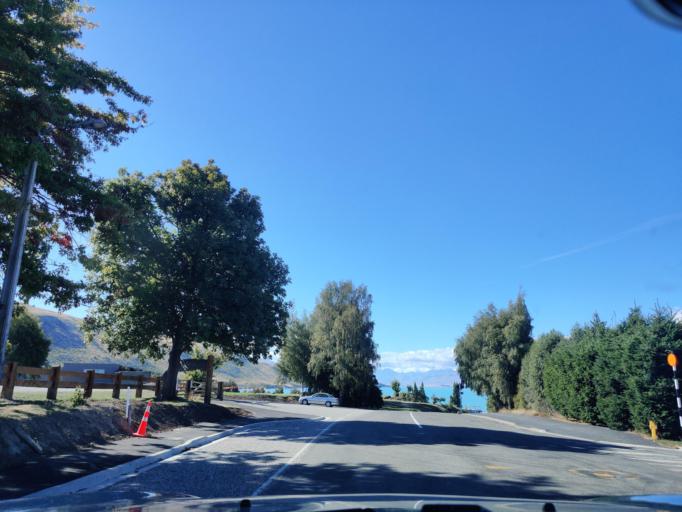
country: NZ
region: Canterbury
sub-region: Timaru District
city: Pleasant Point
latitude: -44.0051
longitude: 170.4752
